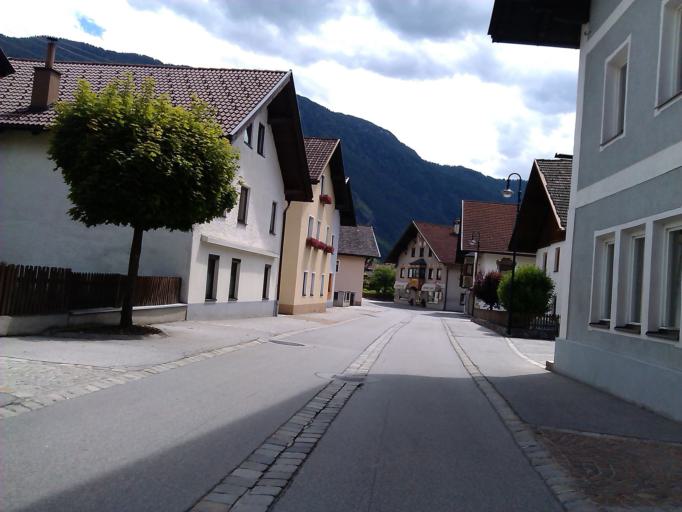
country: AT
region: Tyrol
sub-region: Politischer Bezirk Imst
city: Nassereith
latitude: 47.3132
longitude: 10.8395
